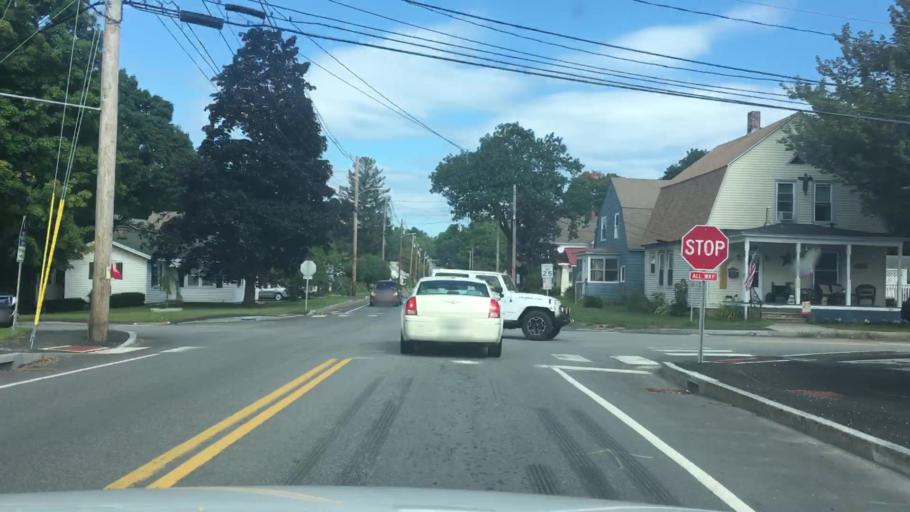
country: US
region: Maine
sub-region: Androscoggin County
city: Auburn
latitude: 44.1047
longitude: -70.2482
